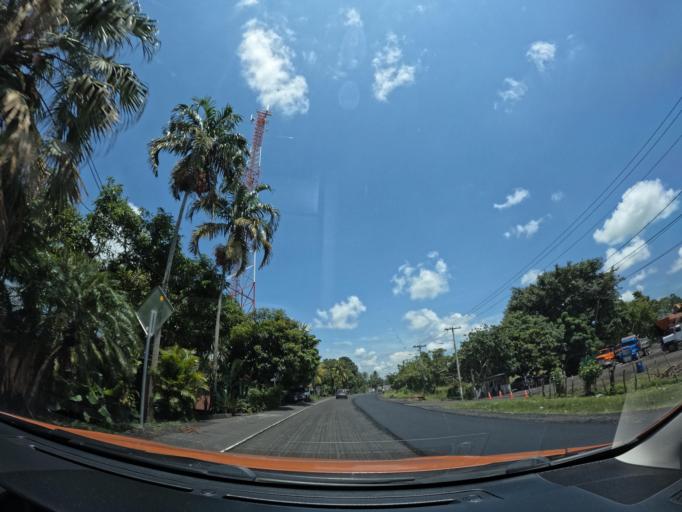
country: GT
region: Escuintla
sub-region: Municipio de Masagua
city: Masagua
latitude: 14.1985
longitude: -90.8526
